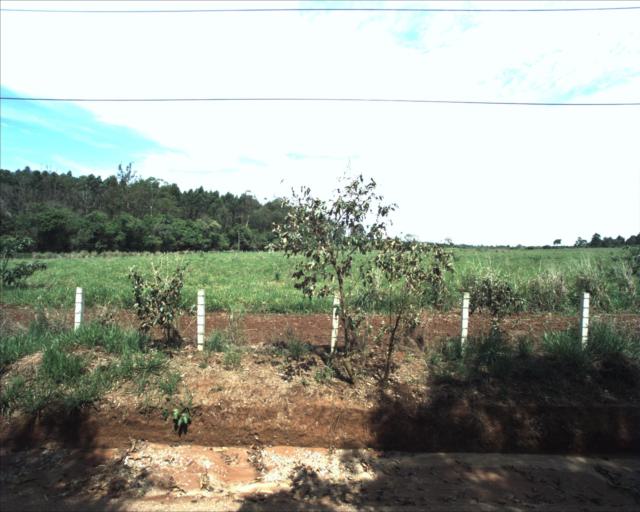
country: BR
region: Sao Paulo
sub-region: Aracoiaba Da Serra
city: Aracoiaba da Serra
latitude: -23.5529
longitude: -47.5467
